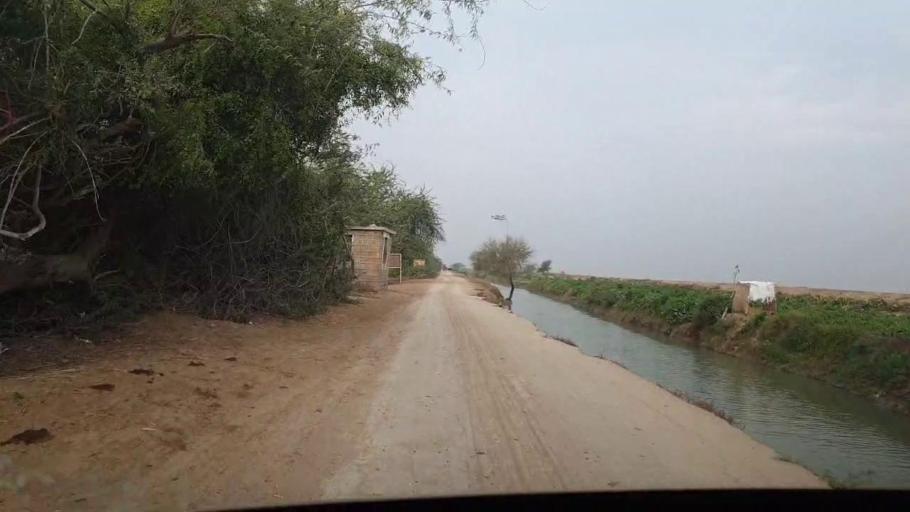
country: PK
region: Sindh
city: Chuhar Jamali
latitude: 24.3998
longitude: 67.9670
